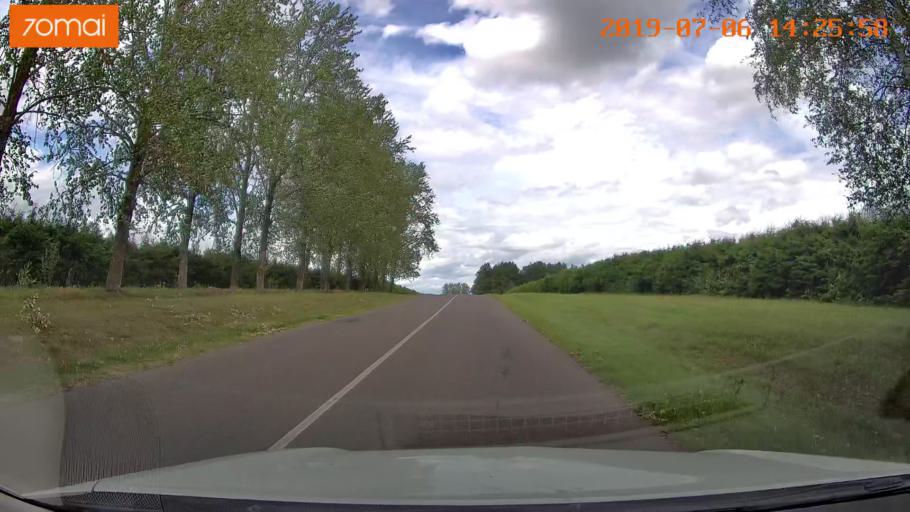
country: BY
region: Minsk
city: Ivyanyets
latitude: 53.9351
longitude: 26.7970
